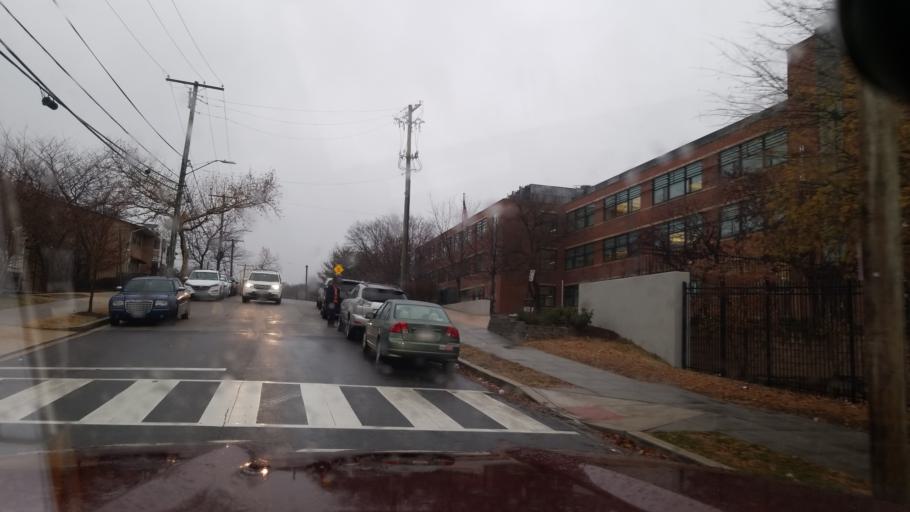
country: US
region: Maryland
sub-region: Prince George's County
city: Hillcrest Heights
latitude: 38.8565
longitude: -76.9892
